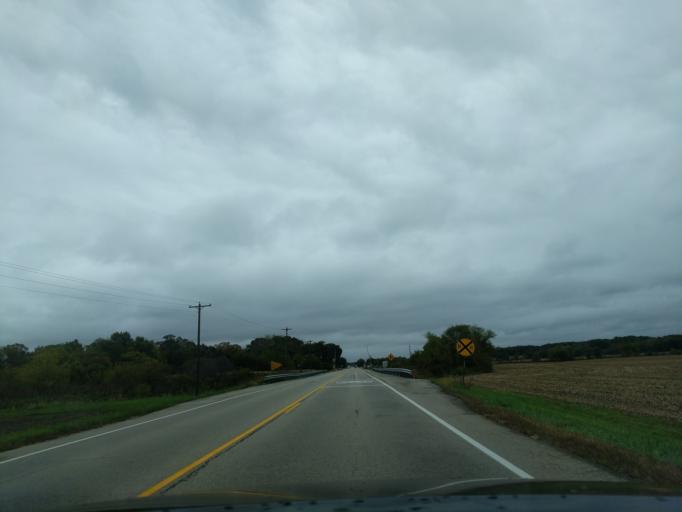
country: US
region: Illinois
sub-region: Ogle County
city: Oregon
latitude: 42.0034
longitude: -89.3679
